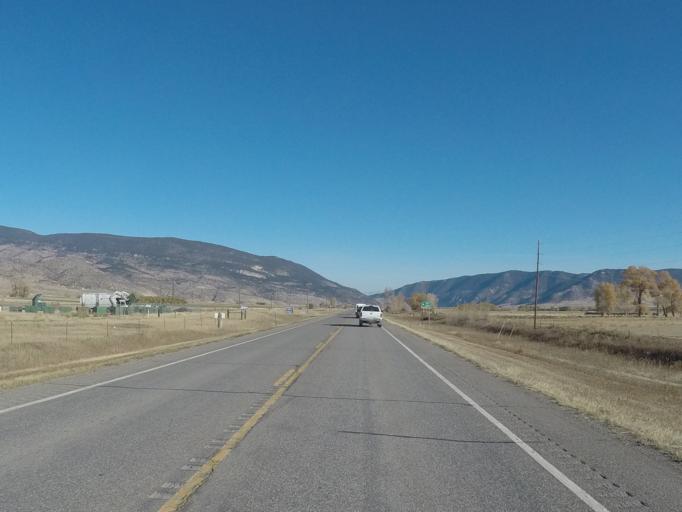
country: US
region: Montana
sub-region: Park County
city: Livingston
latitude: 45.5242
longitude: -110.6079
